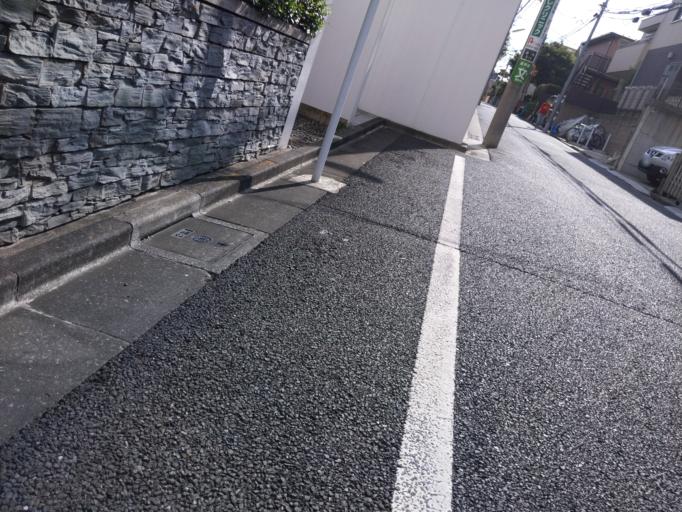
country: JP
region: Tokyo
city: Mitaka-shi
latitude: 35.6518
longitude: 139.6257
